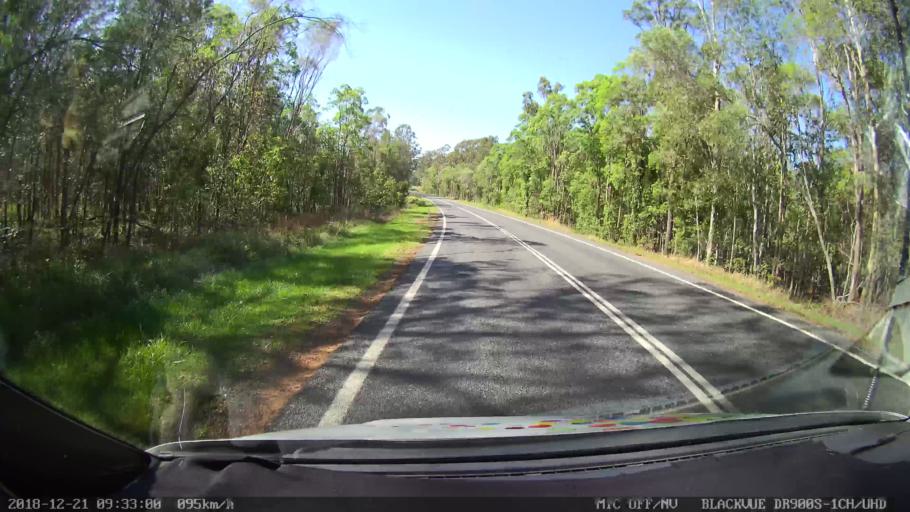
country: AU
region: New South Wales
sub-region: Clarence Valley
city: Grafton
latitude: -29.4782
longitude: 152.9762
